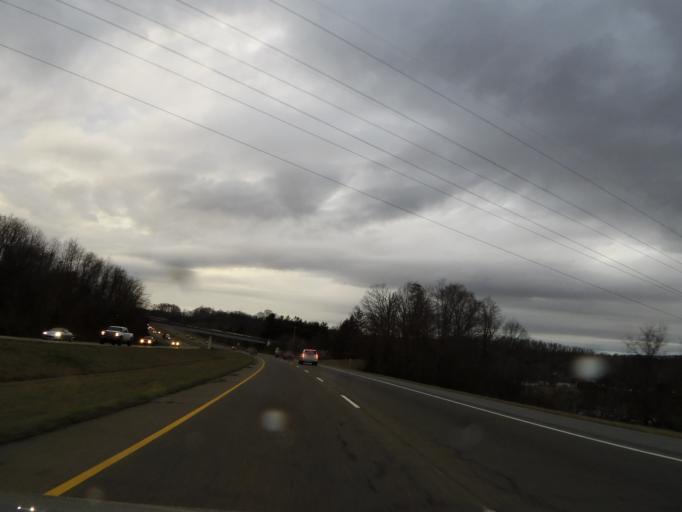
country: US
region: Tennessee
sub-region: Carter County
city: Central
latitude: 36.3159
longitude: -82.3016
